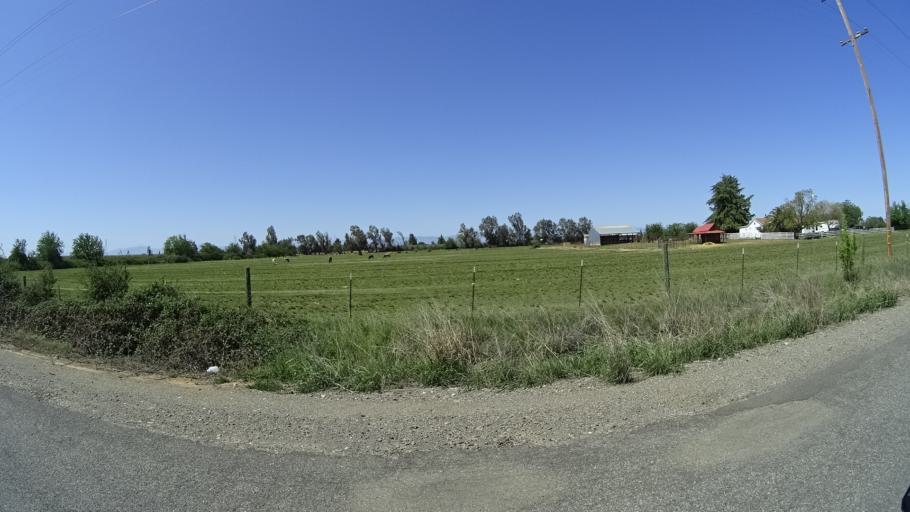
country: US
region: California
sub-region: Glenn County
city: Orland
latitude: 39.7927
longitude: -122.1410
